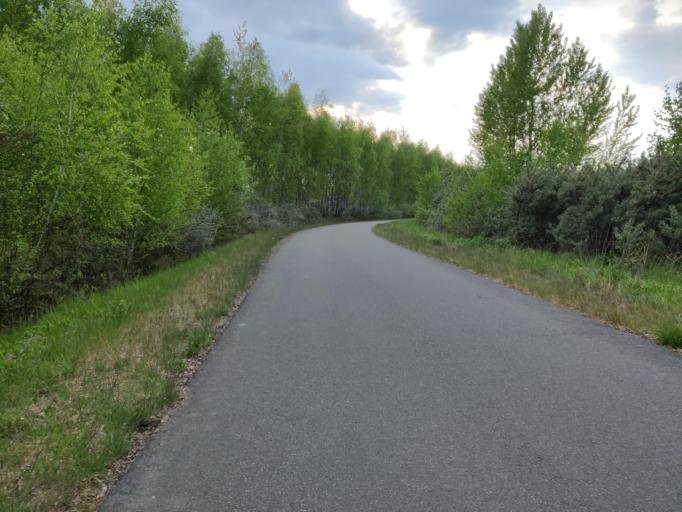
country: DE
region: Saxony
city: Rotha
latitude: 51.2452
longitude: 12.4369
